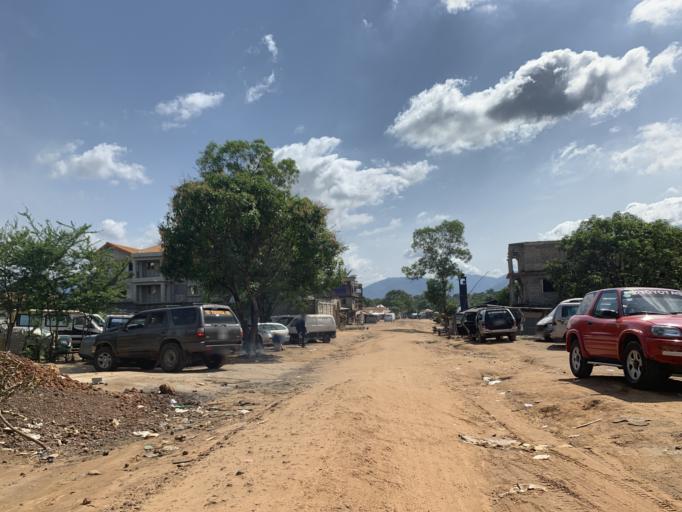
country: SL
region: Western Area
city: Waterloo
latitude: 8.3313
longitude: -13.0507
